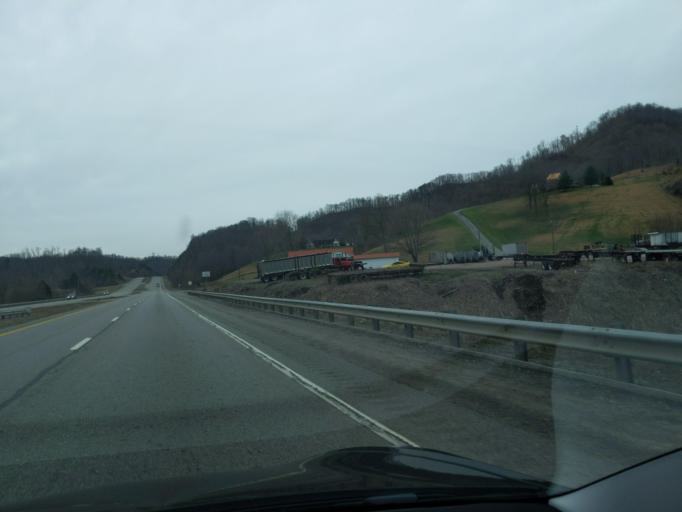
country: US
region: Kentucky
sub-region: Bell County
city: Pineville
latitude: 36.8130
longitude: -83.7655
